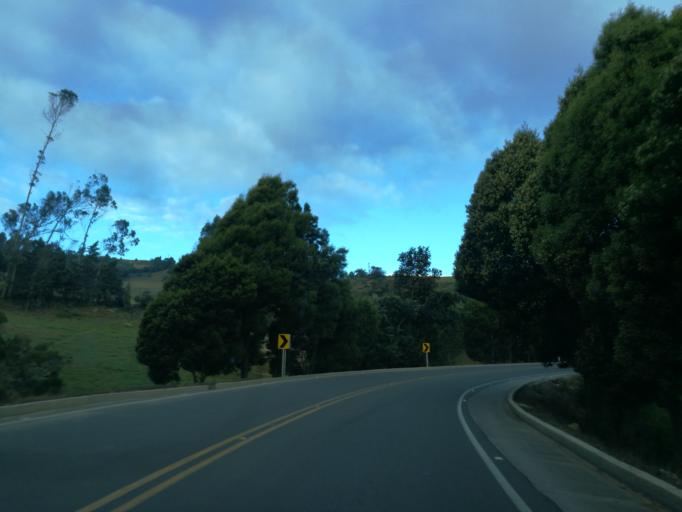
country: CO
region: Boyaca
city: Cucaita
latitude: 5.5601
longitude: -73.4112
